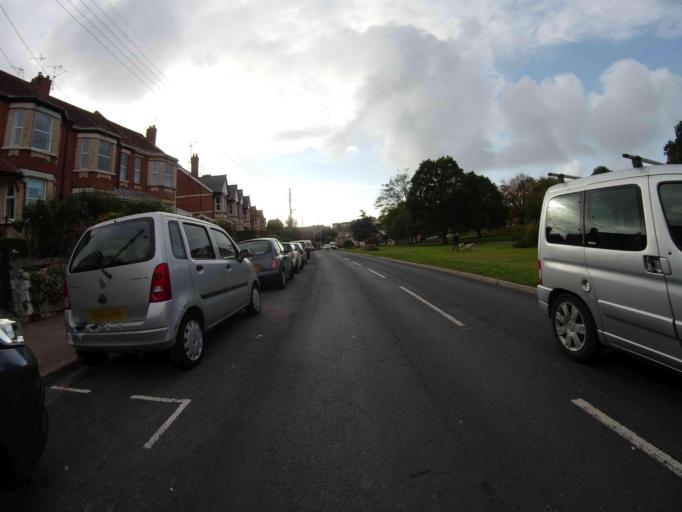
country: GB
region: England
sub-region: Devon
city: Budleigh Salterton
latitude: 50.6326
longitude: -3.3294
